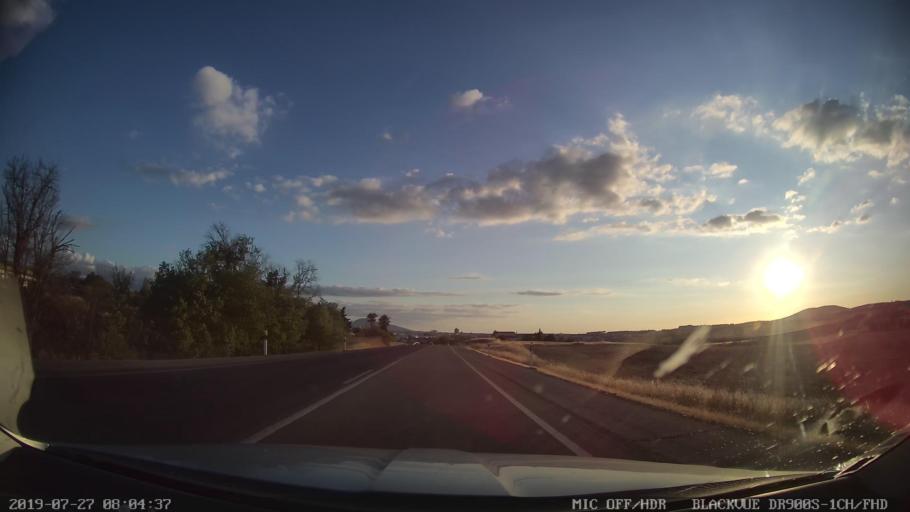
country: ES
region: Extremadura
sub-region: Provincia de Badajoz
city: Merida
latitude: 38.9307
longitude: -6.3139
